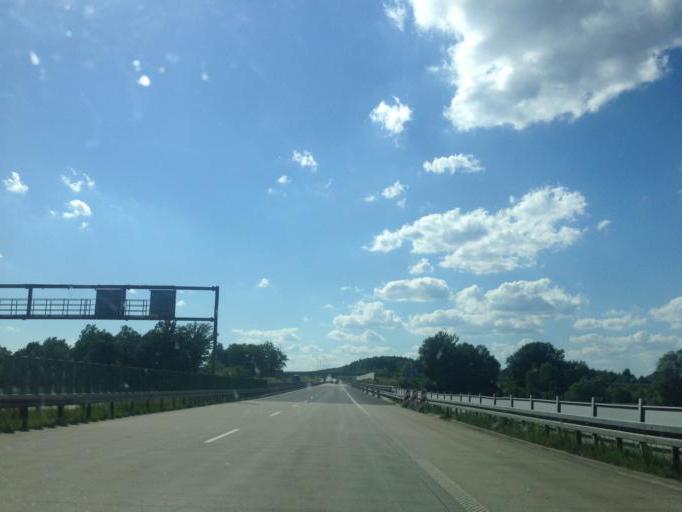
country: PL
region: Lower Silesian Voivodeship
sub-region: Powiat boleslawiecki
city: Nowogrodziec
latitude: 51.2686
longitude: 15.4180
